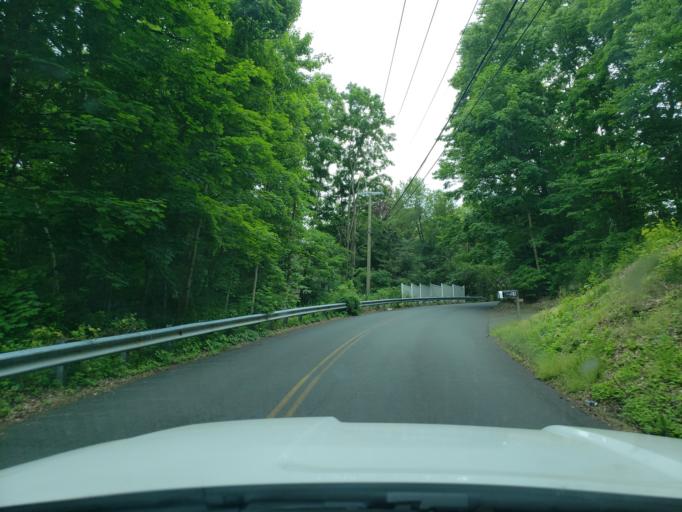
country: US
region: Connecticut
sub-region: Fairfield County
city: Georgetown
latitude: 41.2551
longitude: -73.4366
